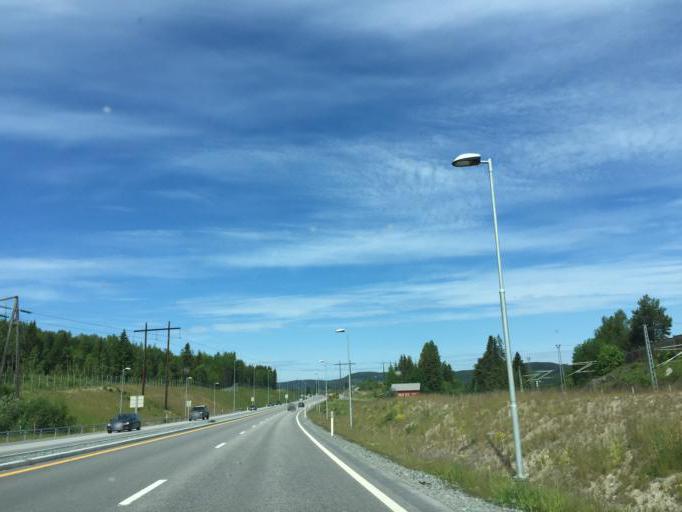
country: NO
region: Hedmark
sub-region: Kongsvinger
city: Kongsvinger
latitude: 60.1908
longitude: 11.9849
